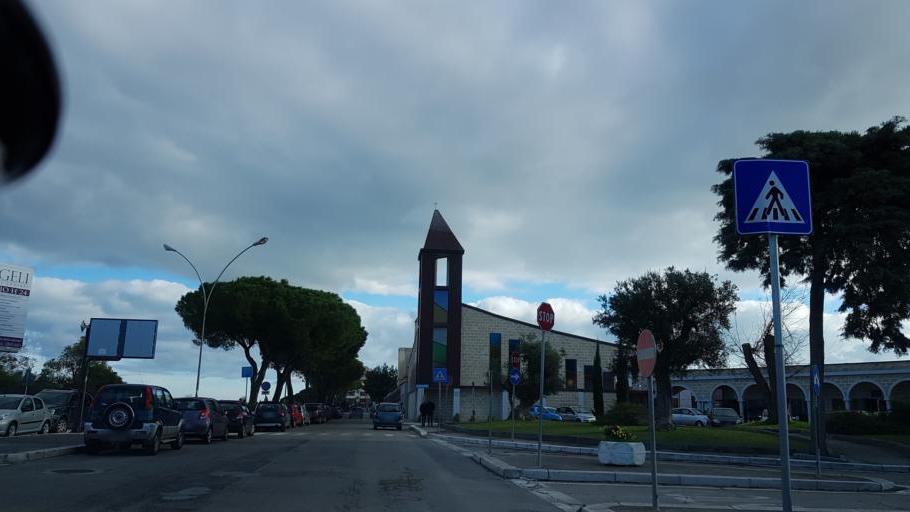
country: IT
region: Apulia
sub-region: Provincia di Brindisi
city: Brindisi
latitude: 40.6290
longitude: 17.9481
